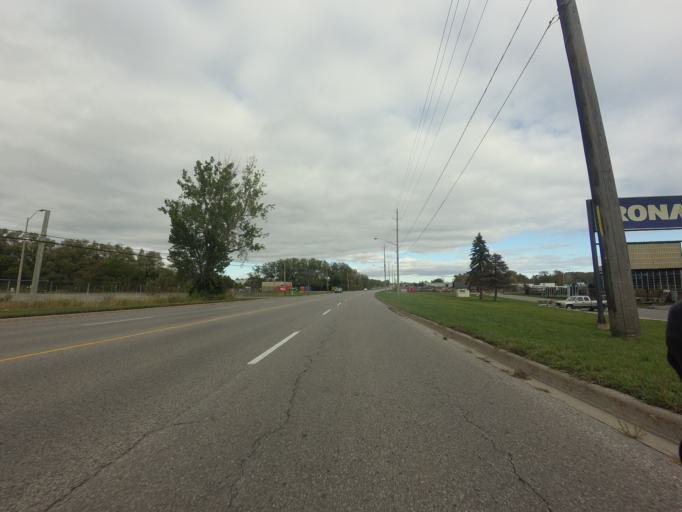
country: CA
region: Ontario
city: Cobourg
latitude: 43.9539
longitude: -78.2733
